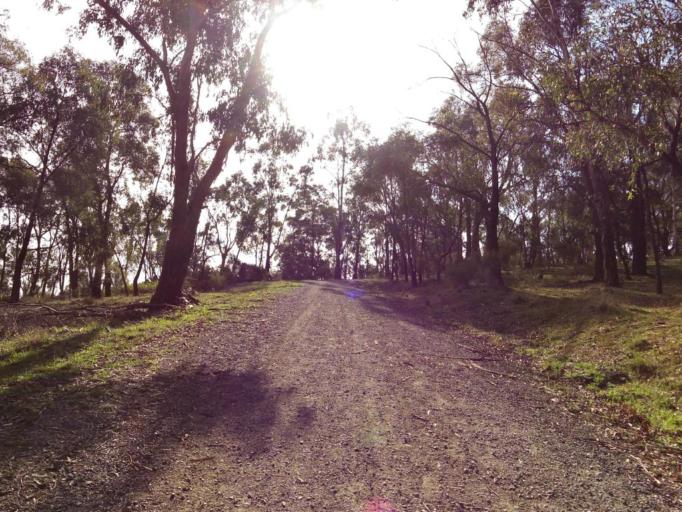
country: AU
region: Victoria
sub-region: Casey
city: Endeavour Hills
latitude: -37.9447
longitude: 145.2665
